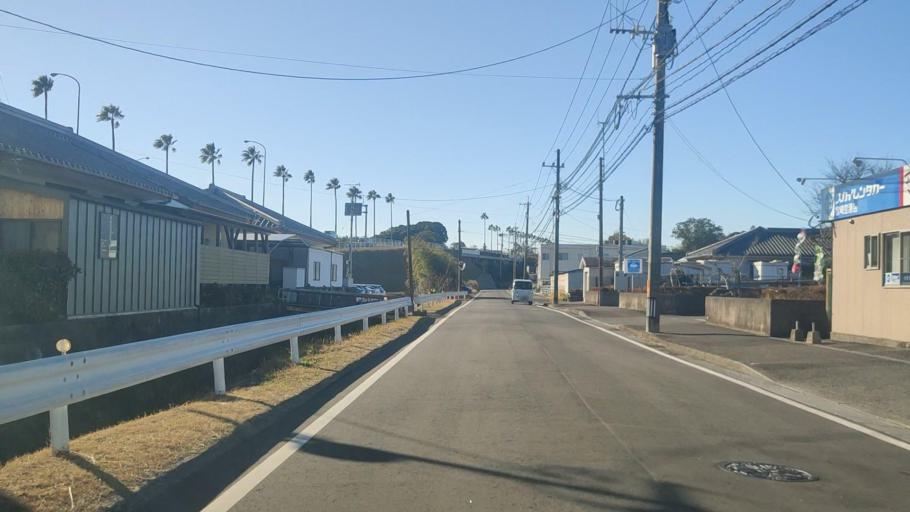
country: JP
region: Miyazaki
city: Miyazaki-shi
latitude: 31.8676
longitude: 131.4347
